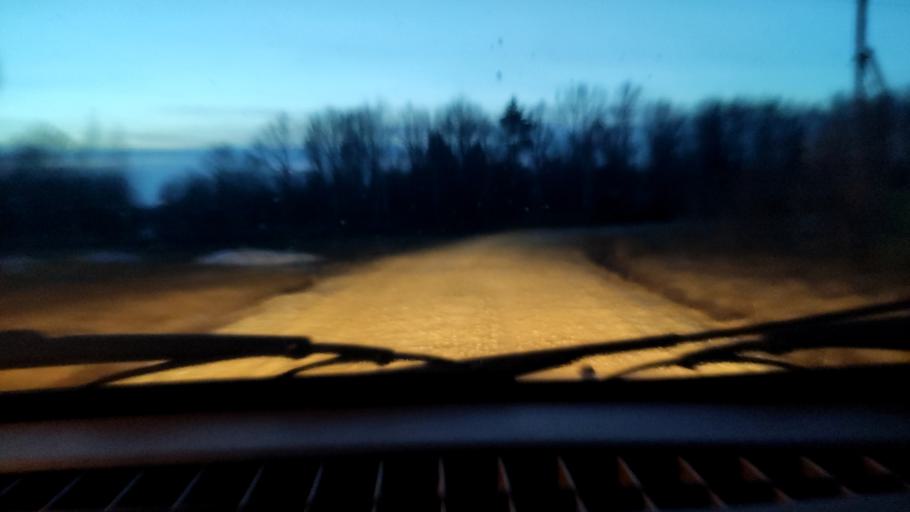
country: RU
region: Bashkortostan
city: Iglino
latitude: 54.7942
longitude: 56.3096
